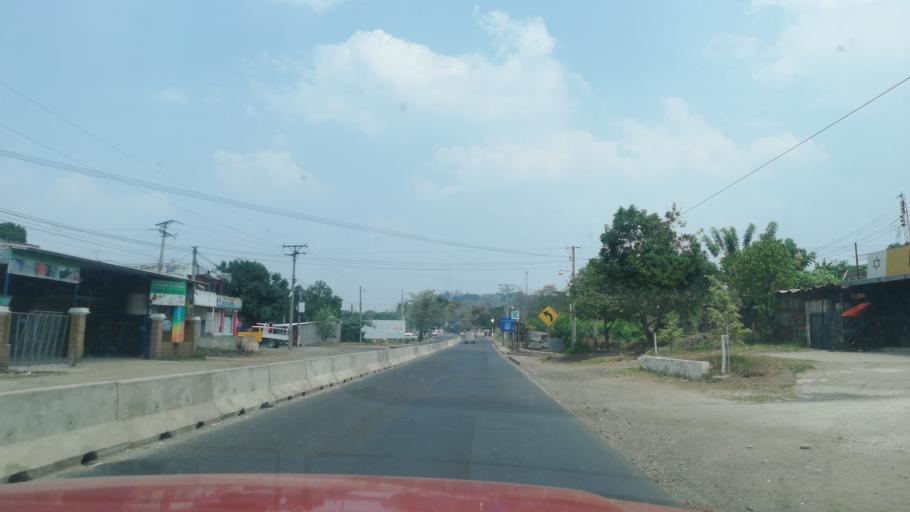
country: SV
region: Santa Ana
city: Santa Ana
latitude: 13.9749
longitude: -89.5875
